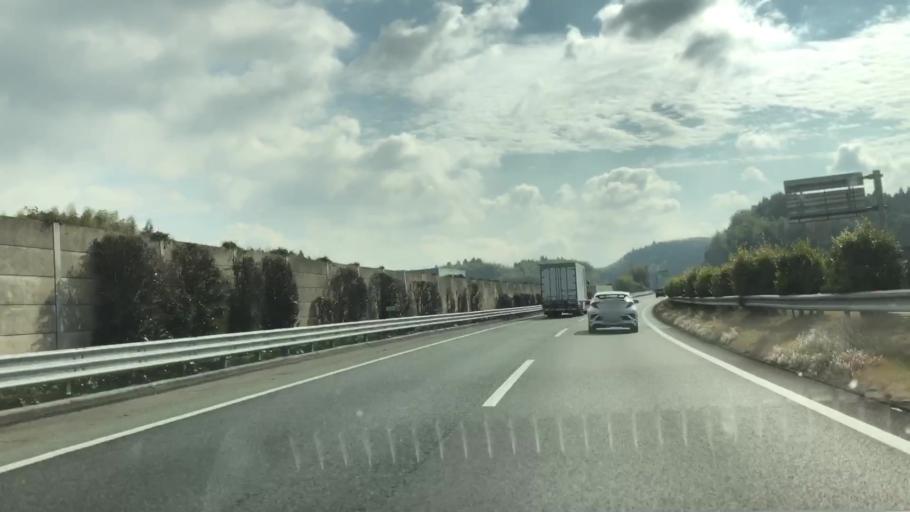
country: JP
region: Fukuoka
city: Setakamachi-takayanagi
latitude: 33.0843
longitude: 130.5416
